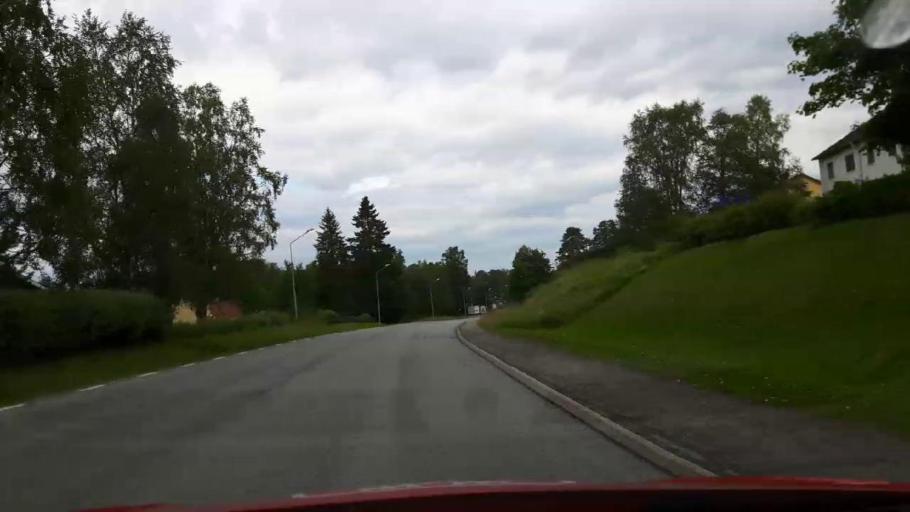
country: SE
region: Jaemtland
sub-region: Stroemsunds Kommun
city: Stroemsund
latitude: 63.5778
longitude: 15.3514
